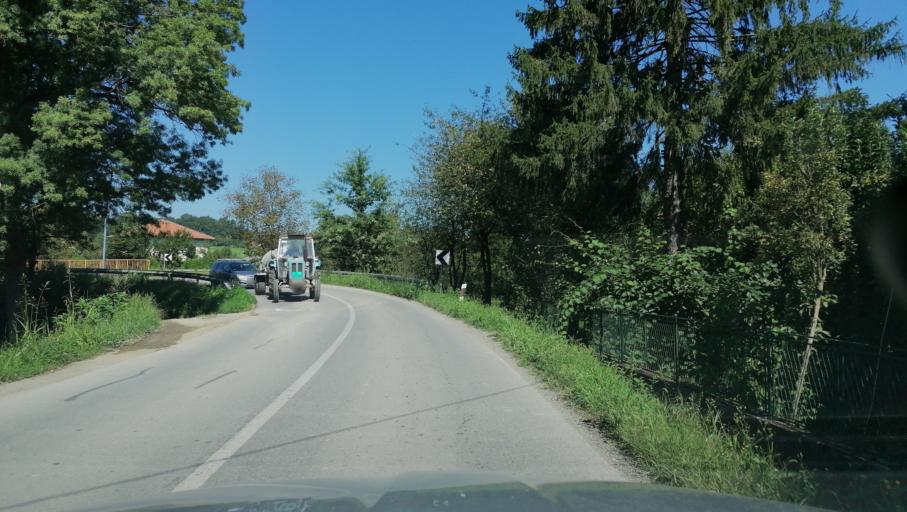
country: RS
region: Central Serbia
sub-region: Raski Okrug
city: Vrnjacka Banja
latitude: 43.7146
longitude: 20.8298
